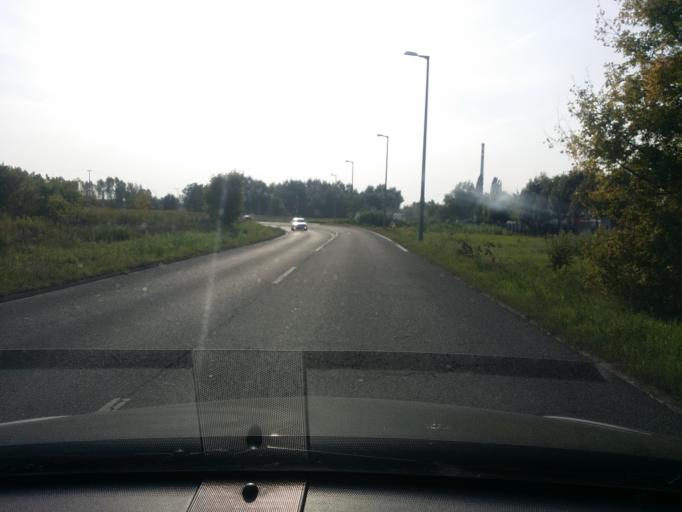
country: HU
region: Budapest
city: Budapest XV. keruelet
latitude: 47.5894
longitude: 19.1266
